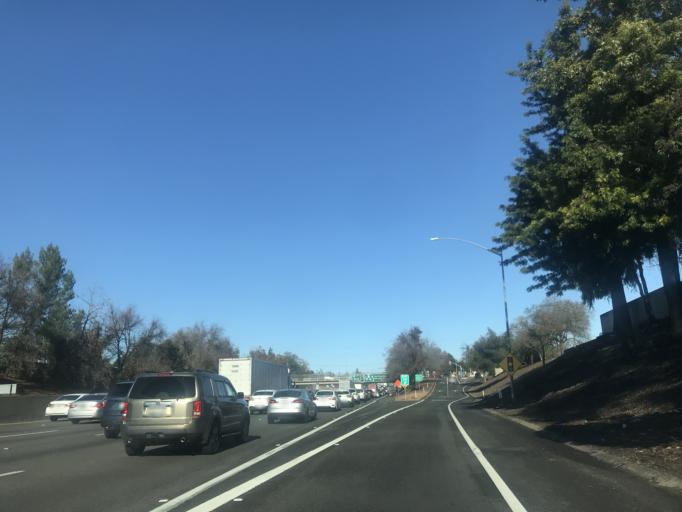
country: US
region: California
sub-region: Sacramento County
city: Parkway
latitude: 38.5389
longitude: -121.4735
